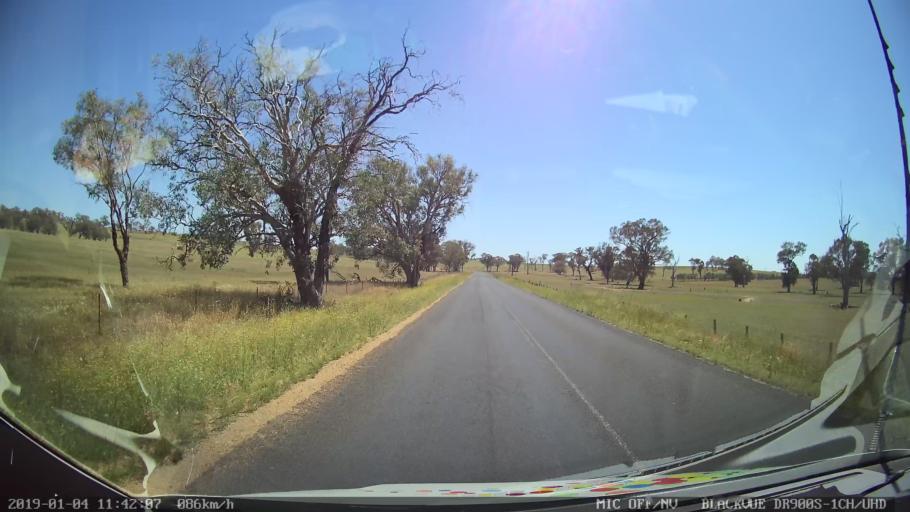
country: AU
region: New South Wales
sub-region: Cabonne
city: Molong
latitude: -32.9855
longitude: 148.7866
